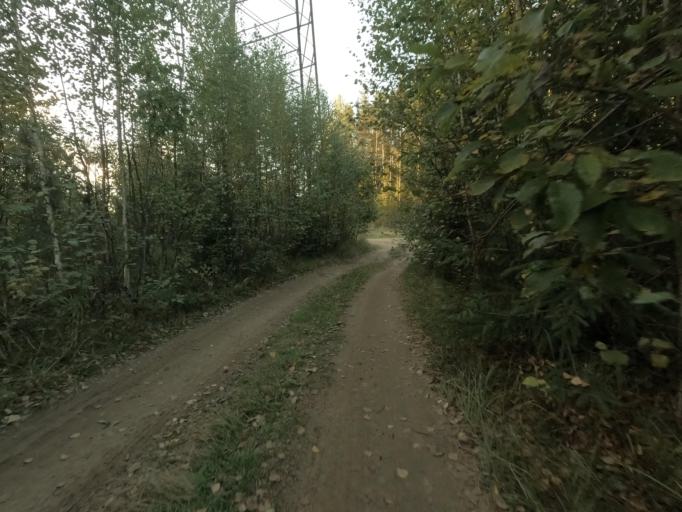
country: RU
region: Leningrad
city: Otradnoye
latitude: 59.8233
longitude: 30.8228
